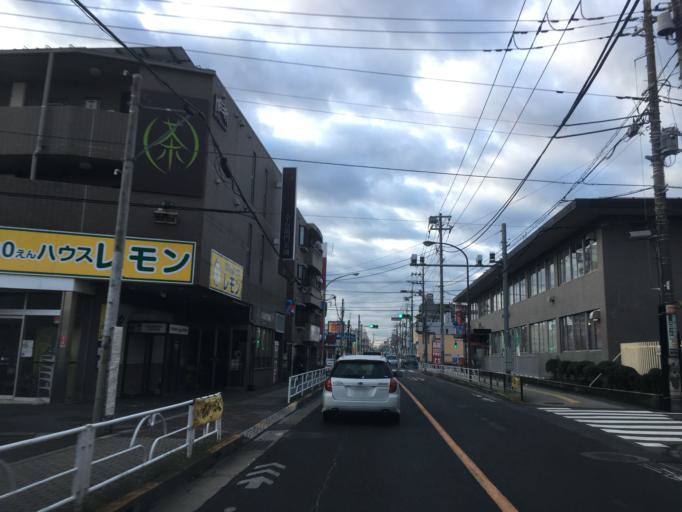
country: JP
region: Tokyo
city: Higashimurayama-shi
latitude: 35.7587
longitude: 139.4671
